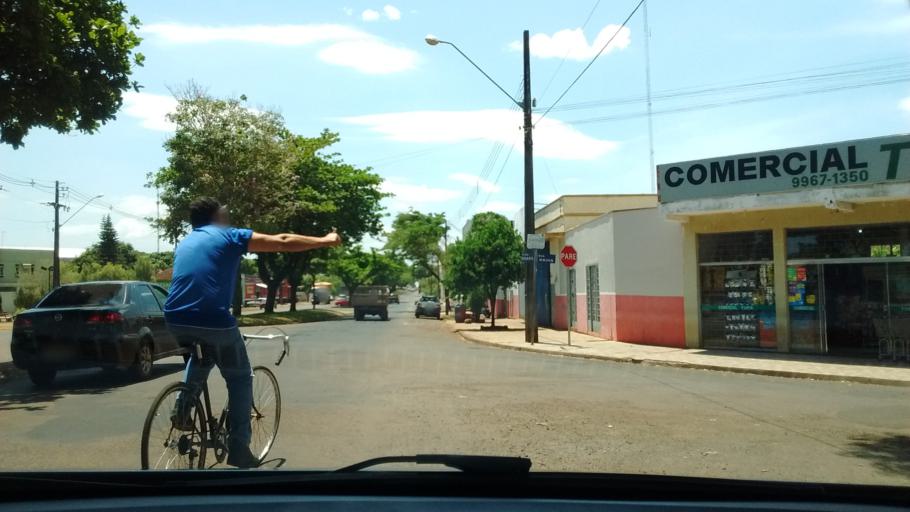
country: BR
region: Parana
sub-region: Corbelia
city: Corbelia
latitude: -24.5351
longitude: -52.9966
